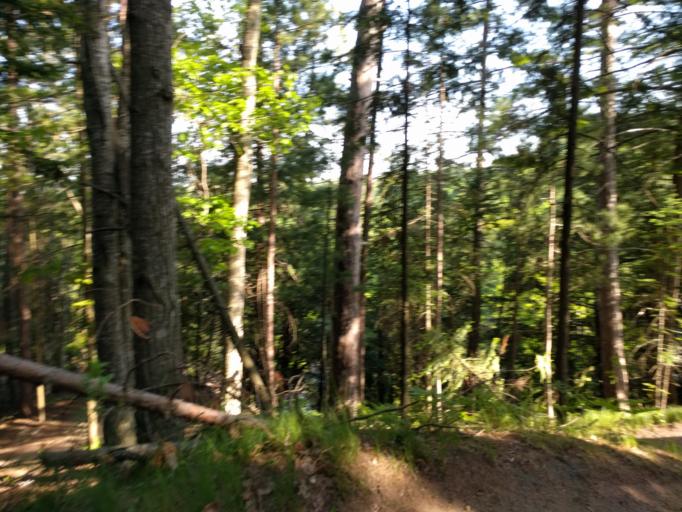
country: US
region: Michigan
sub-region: Marquette County
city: Trowbridge Park
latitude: 46.5693
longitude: -87.4542
